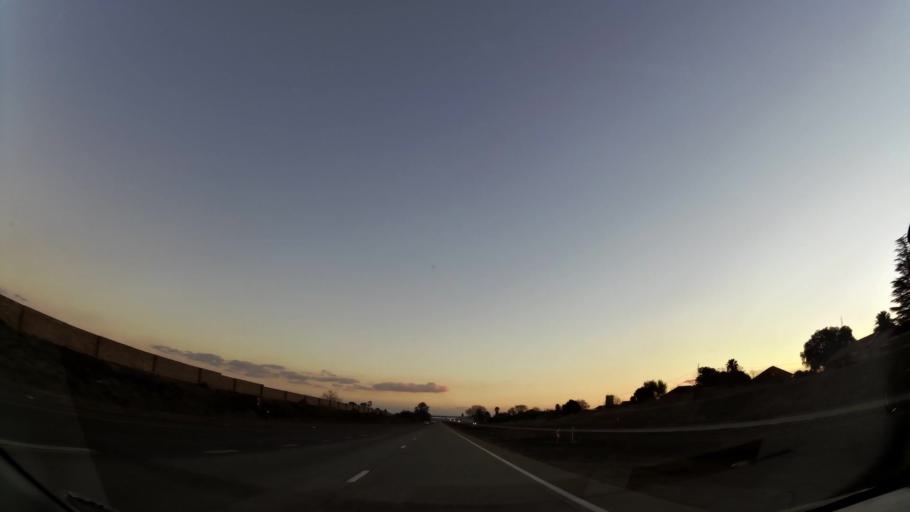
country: ZA
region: Mpumalanga
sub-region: Nkangala District Municipality
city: Witbank
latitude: -25.9212
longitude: 29.2289
